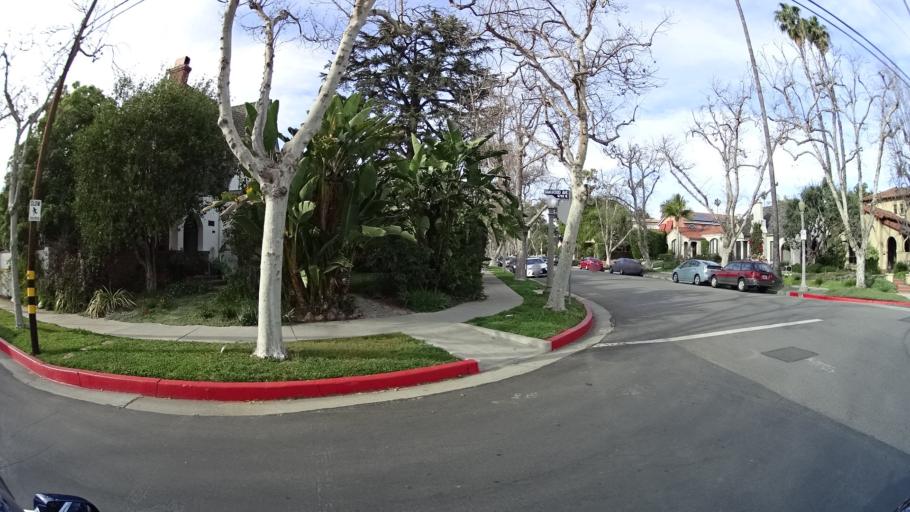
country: US
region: California
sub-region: Los Angeles County
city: Hollywood
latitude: 34.0783
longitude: -118.3398
